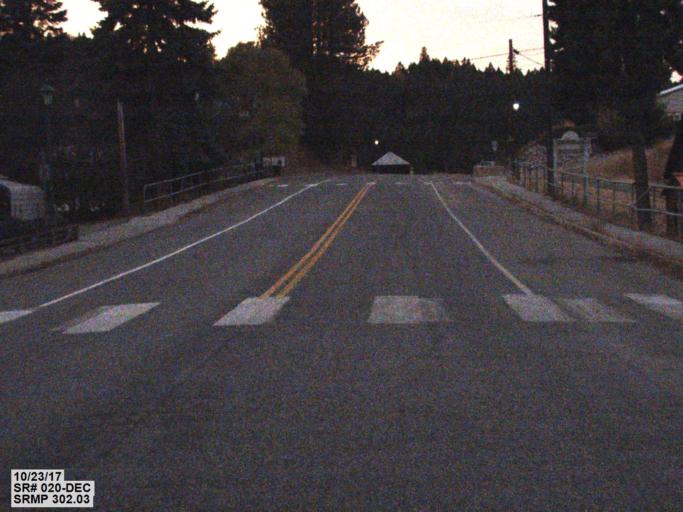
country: US
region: Washington
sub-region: Ferry County
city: Republic
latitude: 48.6476
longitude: -118.7391
